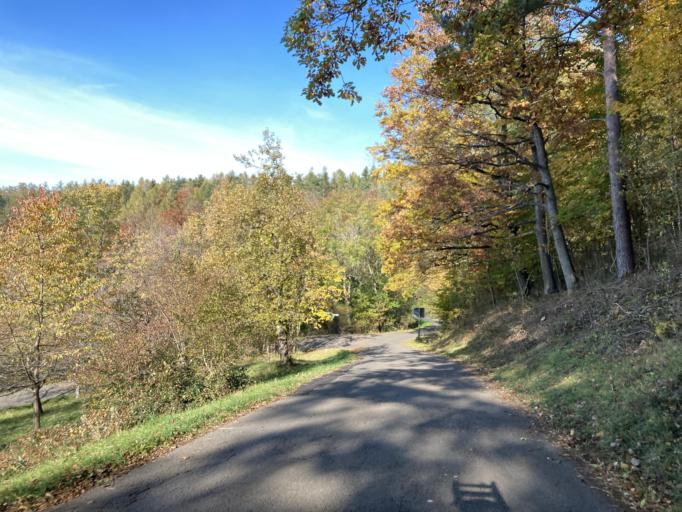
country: DE
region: Baden-Wuerttemberg
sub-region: Tuebingen Region
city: Mossingen
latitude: 48.3879
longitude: 9.0601
